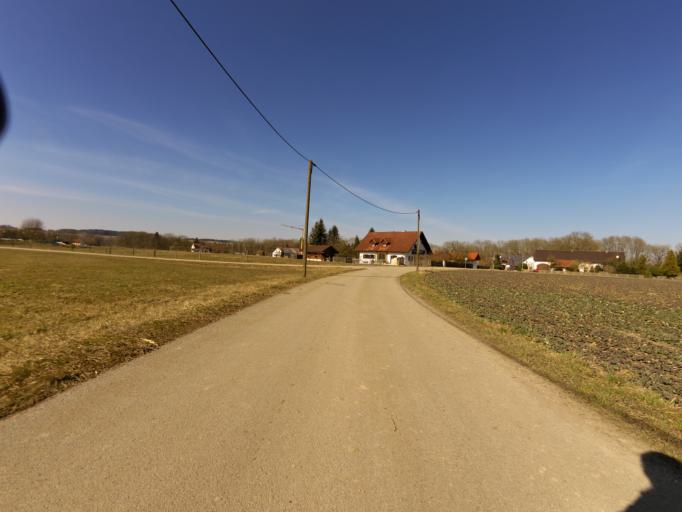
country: DE
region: Bavaria
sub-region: Upper Bavaria
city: Wang
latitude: 48.4938
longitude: 11.9658
